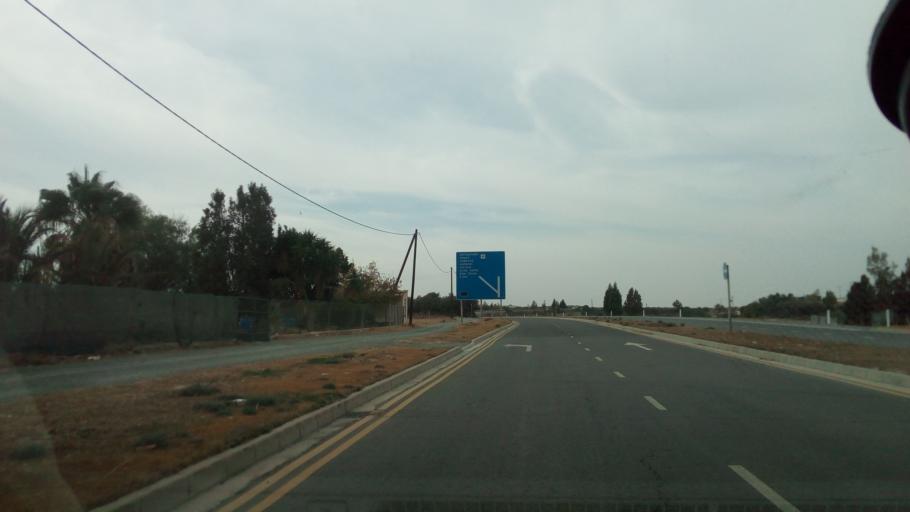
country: CY
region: Larnaka
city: Aradippou
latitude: 34.9272
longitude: 33.5717
